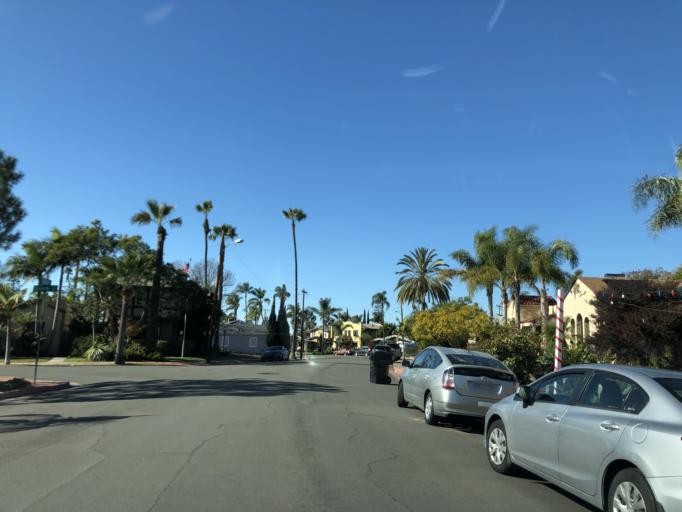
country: US
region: California
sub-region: San Diego County
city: San Diego
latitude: 32.7319
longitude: -117.1265
